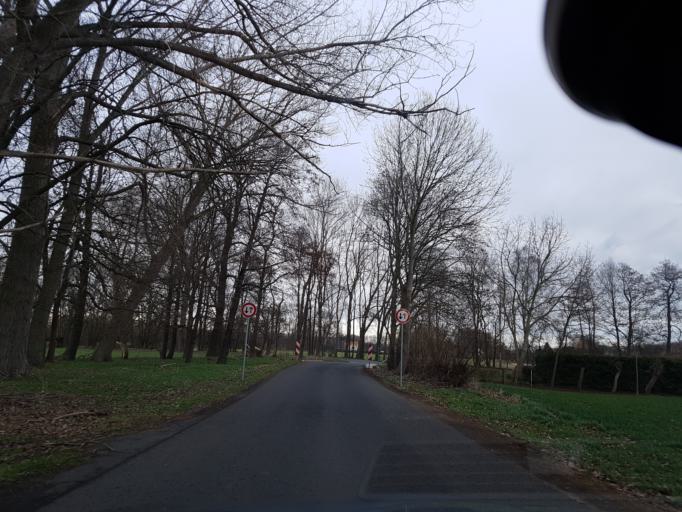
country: DE
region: Saxony
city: Stauchitz
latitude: 51.2543
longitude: 13.2273
